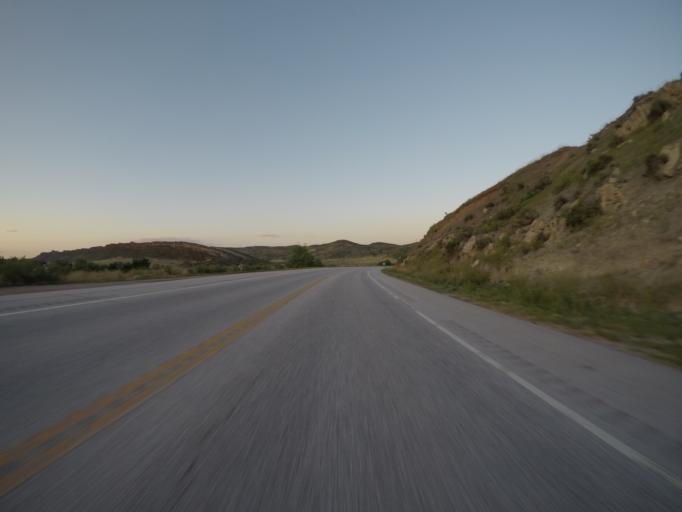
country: US
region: Colorado
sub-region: Larimer County
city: Laporte
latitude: 40.6743
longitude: -105.1873
